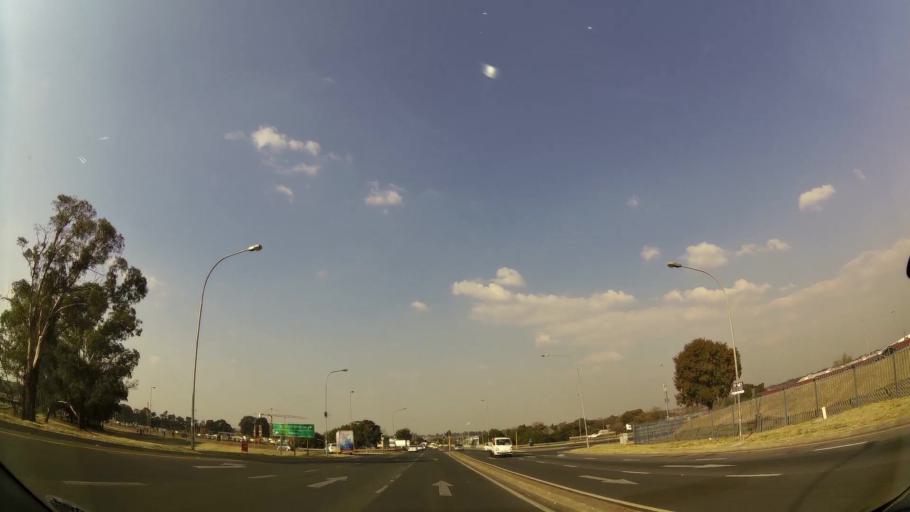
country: ZA
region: Gauteng
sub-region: City of Johannesburg Metropolitan Municipality
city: Modderfontein
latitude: -26.0918
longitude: 28.2666
